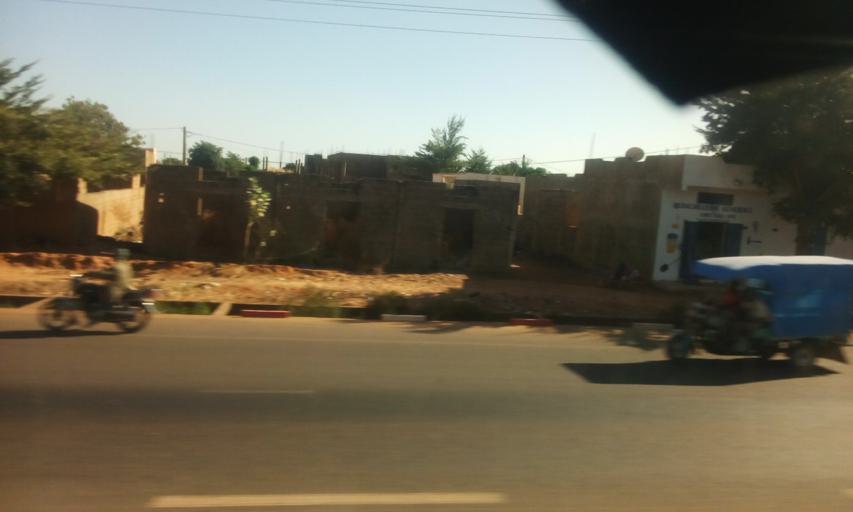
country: ML
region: Segou
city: Segou
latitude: 13.4178
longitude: -6.3074
